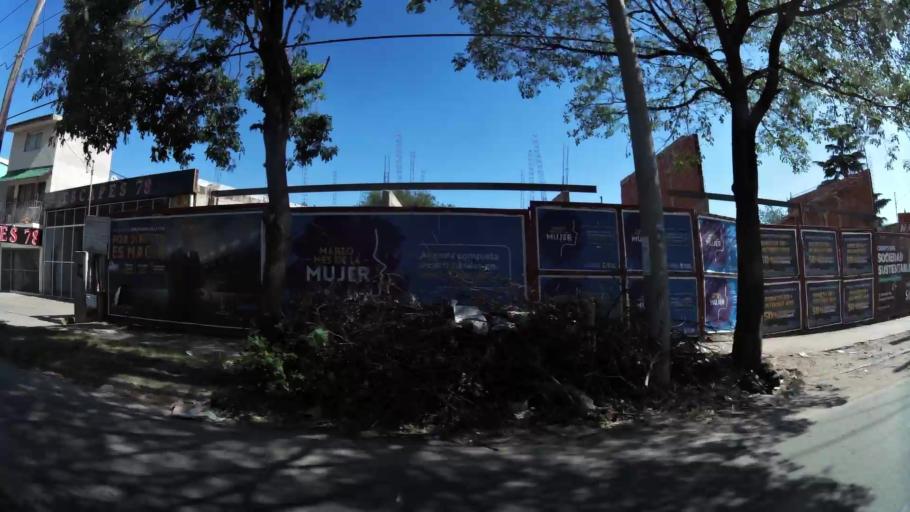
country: AR
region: Cordoba
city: Villa Allende
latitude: -31.3317
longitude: -64.2637
